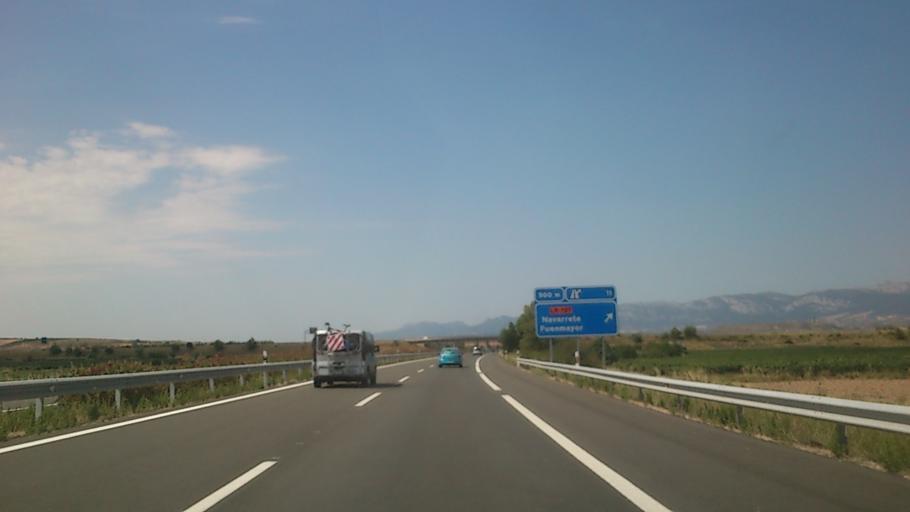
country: ES
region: La Rioja
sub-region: Provincia de La Rioja
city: Navarrete
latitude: 42.4372
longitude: -2.5519
